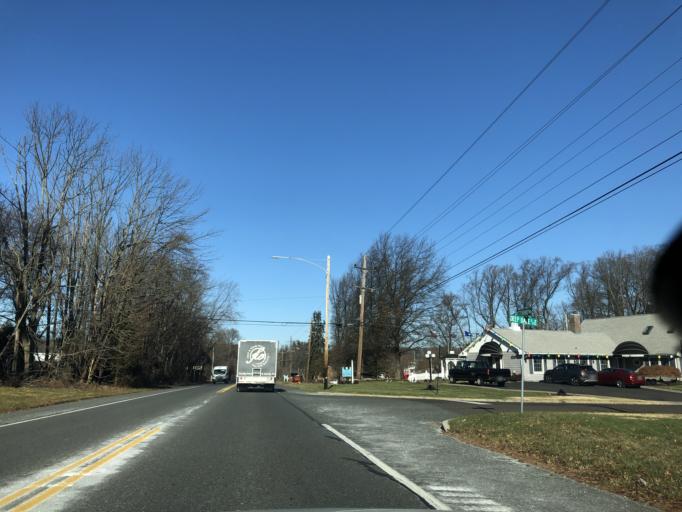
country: US
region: Pennsylvania
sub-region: Bucks County
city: Hulmeville
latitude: 40.1585
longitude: -74.8954
